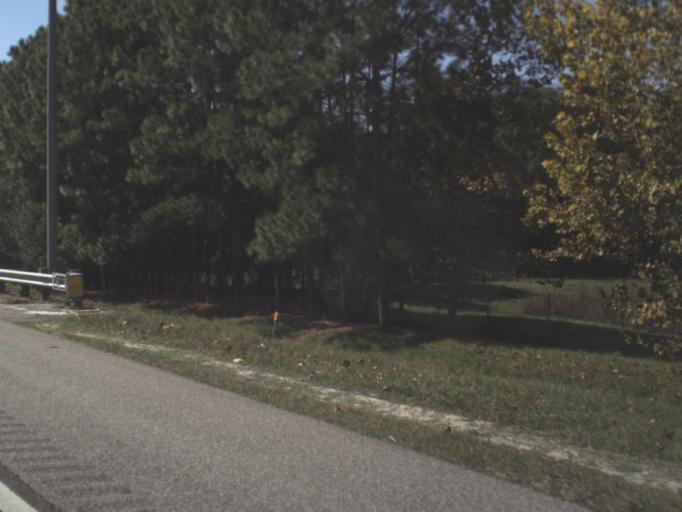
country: US
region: Florida
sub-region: Hillsborough County
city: Citrus Park
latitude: 28.0702
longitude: -82.5650
